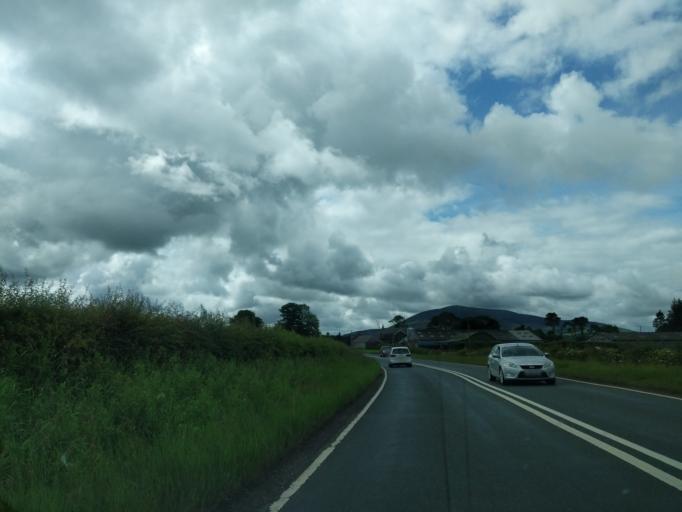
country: GB
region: Scotland
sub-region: South Lanarkshire
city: Biggar
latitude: 55.6106
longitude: -3.5550
